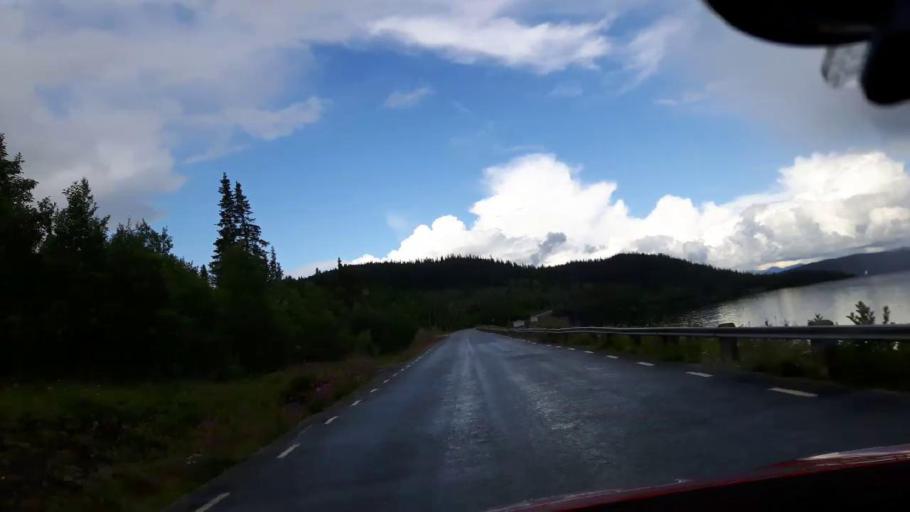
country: SE
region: Vaesterbotten
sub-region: Vilhelmina Kommun
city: Sjoberg
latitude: 64.9810
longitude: 15.3049
